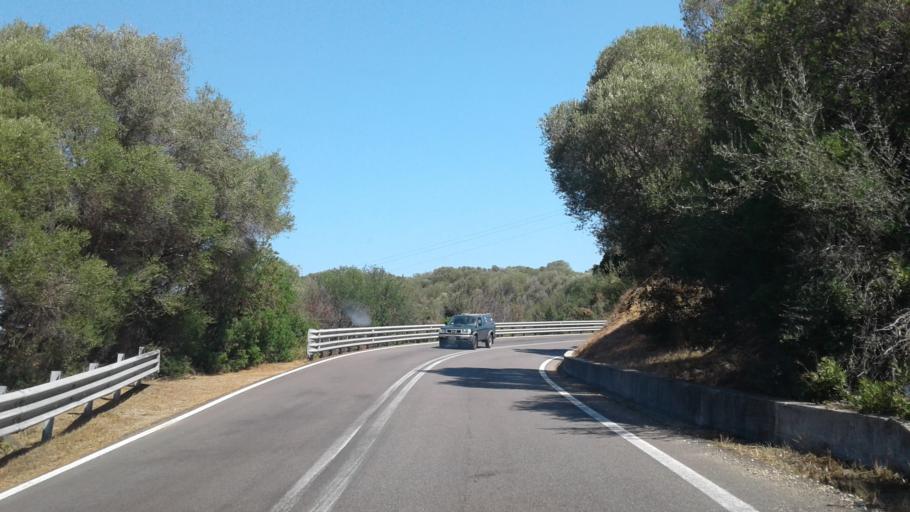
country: IT
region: Sardinia
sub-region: Provincia di Olbia-Tempio
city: Palau
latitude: 41.1678
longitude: 9.3175
